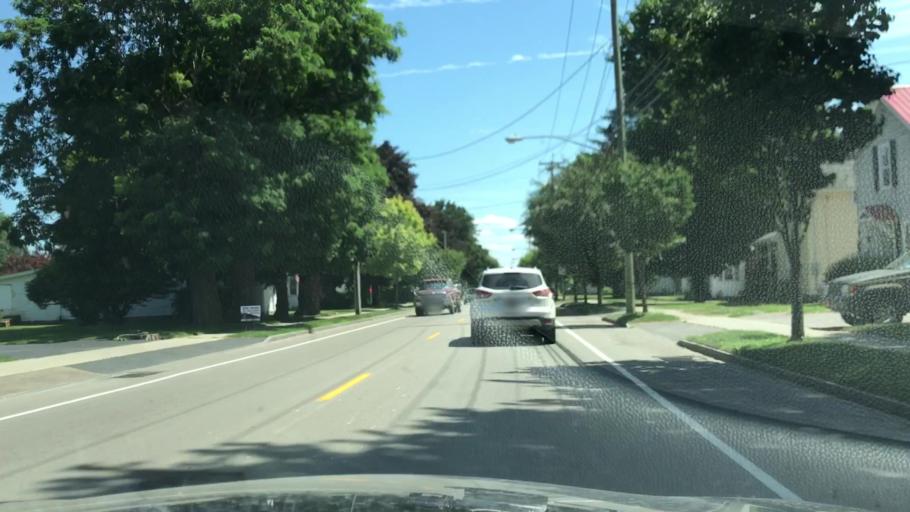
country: US
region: New York
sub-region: Livingston County
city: Mount Morris
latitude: 42.7357
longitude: -77.8801
